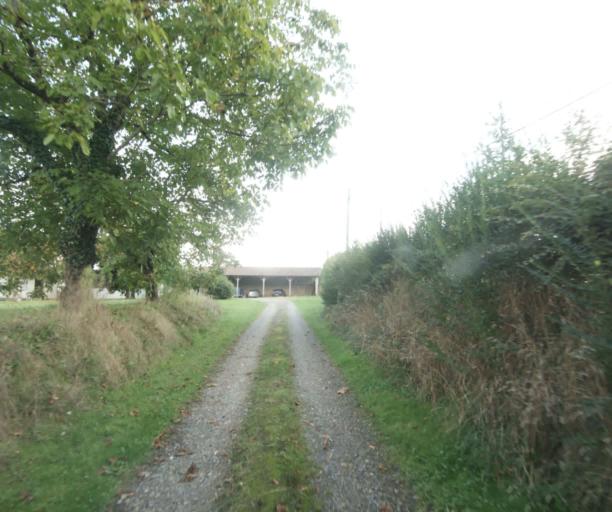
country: FR
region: Midi-Pyrenees
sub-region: Departement du Gers
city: Le Houga
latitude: 43.8438
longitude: -0.1341
